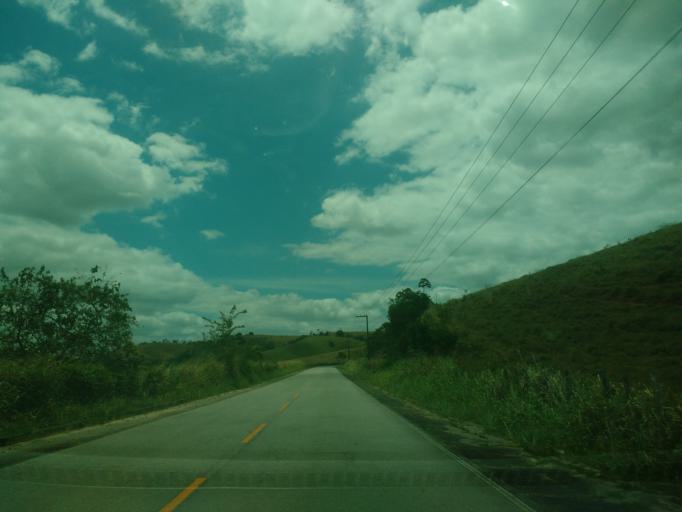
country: BR
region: Alagoas
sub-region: Uniao Dos Palmares
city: Uniao dos Palmares
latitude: -9.1376
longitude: -36.1158
